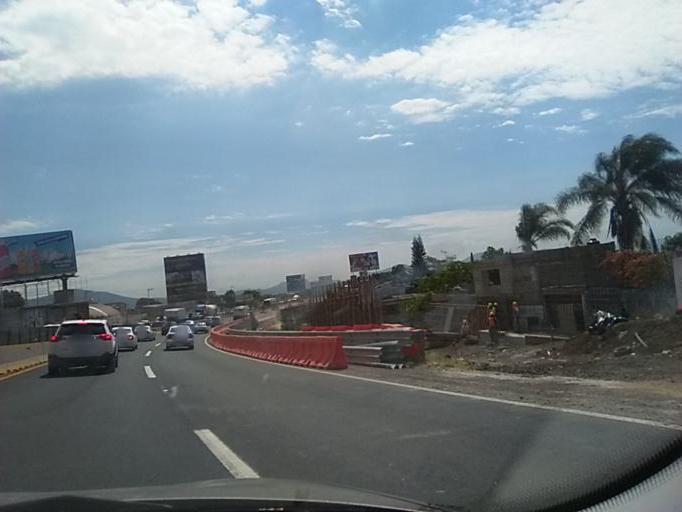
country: MX
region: Morelos
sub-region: Cuernavaca
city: Colonia los Cerritos
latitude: 18.9534
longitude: -99.1925
